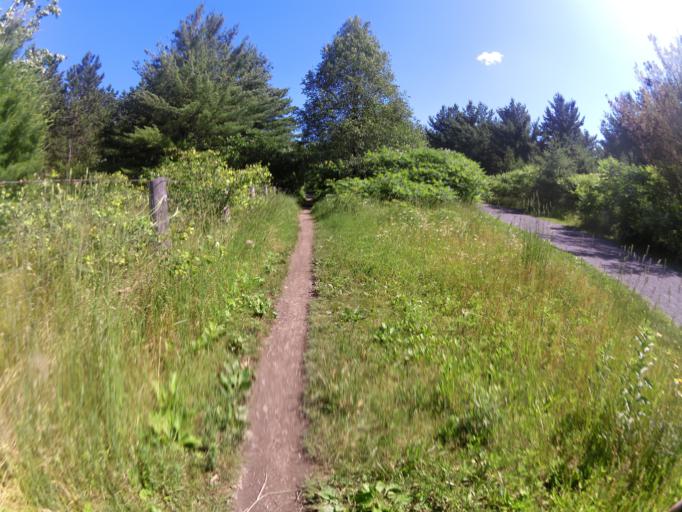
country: CA
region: Ontario
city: Bells Corners
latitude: 45.3240
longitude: -75.7942
